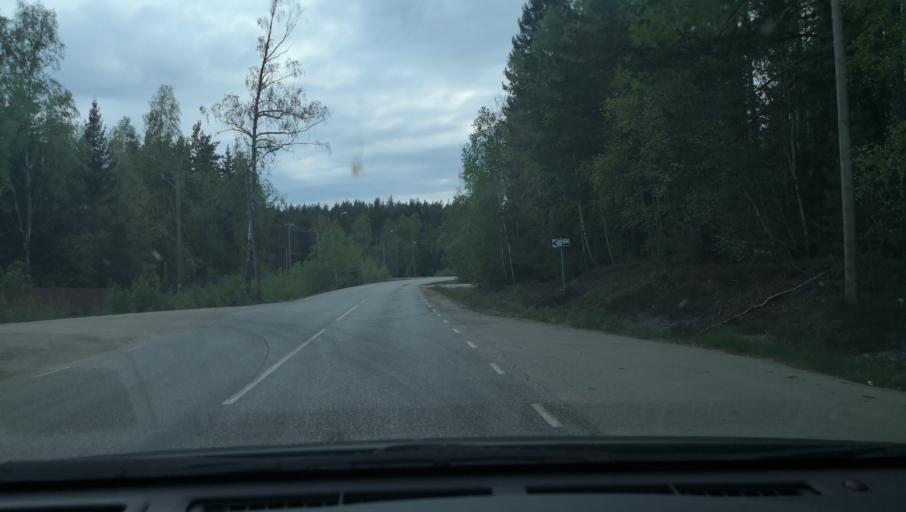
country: SE
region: Vaestmanland
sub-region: Skinnskattebergs Kommun
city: Skinnskatteberg
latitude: 59.8313
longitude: 15.5620
